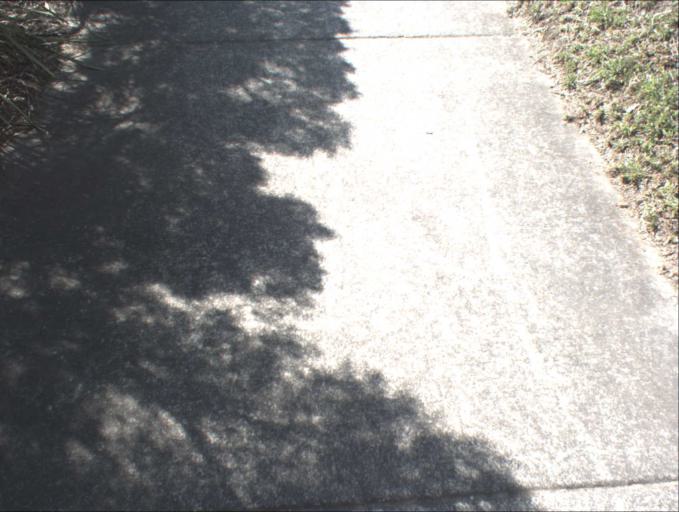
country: AU
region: Queensland
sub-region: Logan
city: Waterford West
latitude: -27.7003
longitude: 153.1584
